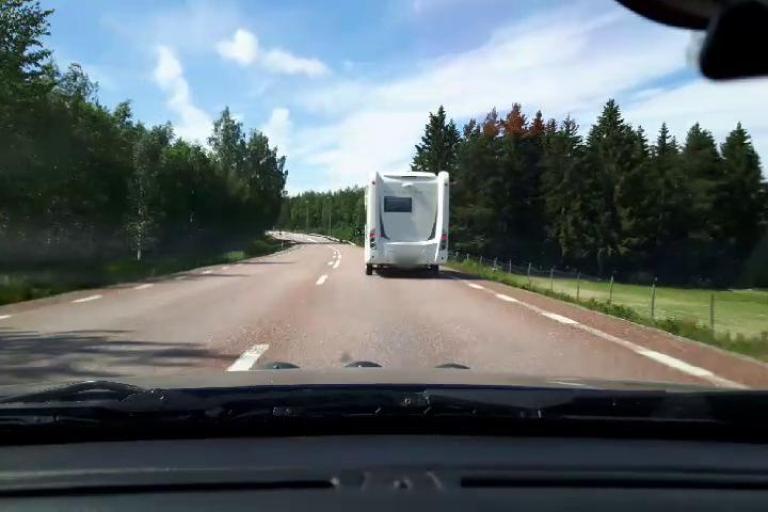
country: SE
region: Gaevleborg
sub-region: Bollnas Kommun
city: Kilafors
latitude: 61.2145
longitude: 16.7346
